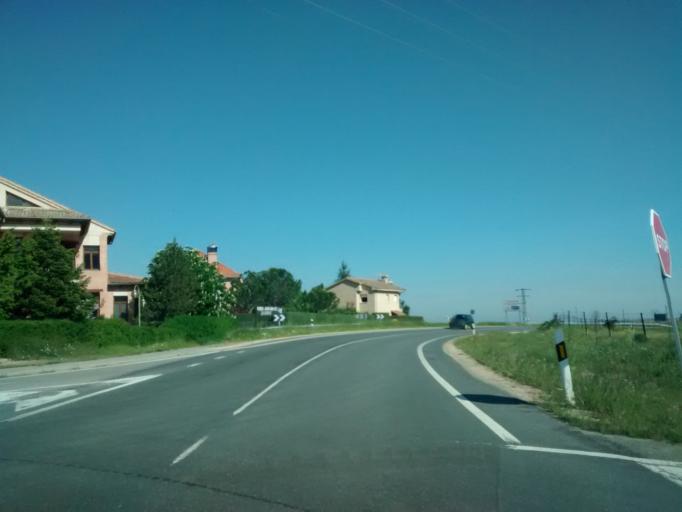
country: ES
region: Castille and Leon
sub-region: Provincia de Segovia
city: Trescasas
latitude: 40.9642
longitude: -4.0334
